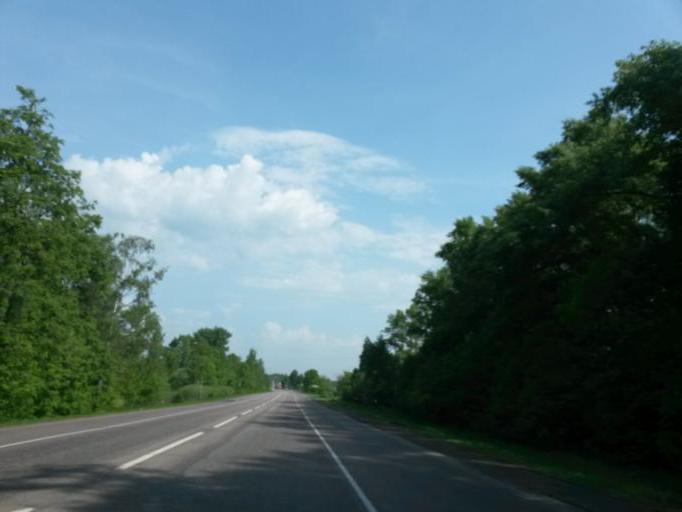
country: RU
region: Moskovskaya
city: Stolbovaya
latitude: 55.2393
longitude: 37.5044
